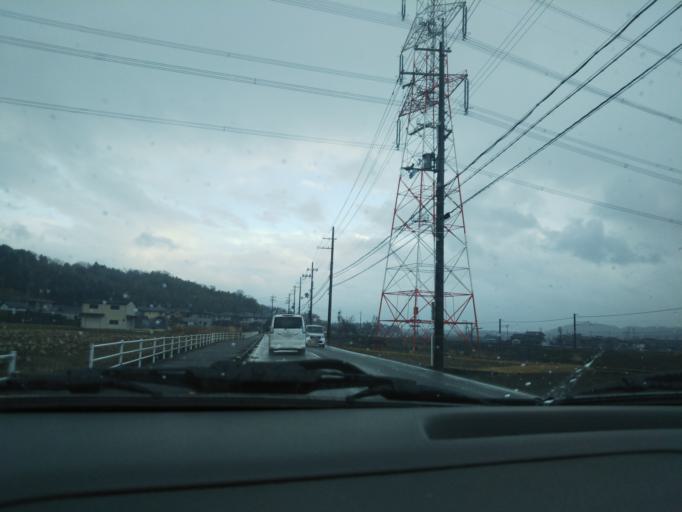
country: JP
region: Shiga Prefecture
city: Minakuchicho-matoba
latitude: 34.9471
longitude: 136.1585
